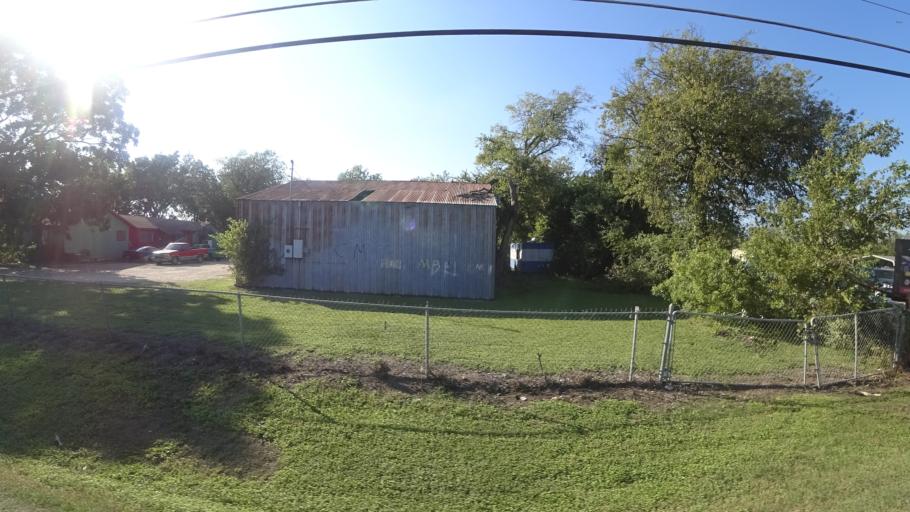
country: US
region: Texas
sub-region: Travis County
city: Wells Branch
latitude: 30.3520
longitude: -97.6689
